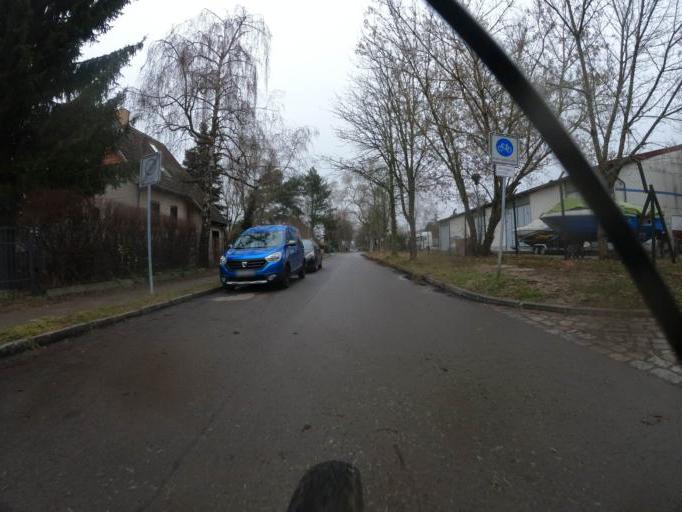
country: DE
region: Berlin
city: Biesdorf
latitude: 52.4870
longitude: 13.5582
